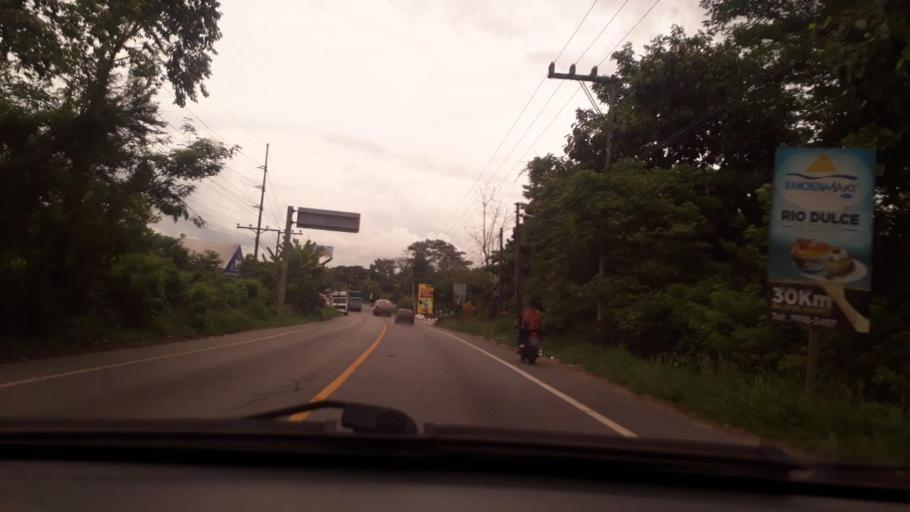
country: GT
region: Izabal
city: Morales
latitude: 15.5004
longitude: -88.8345
